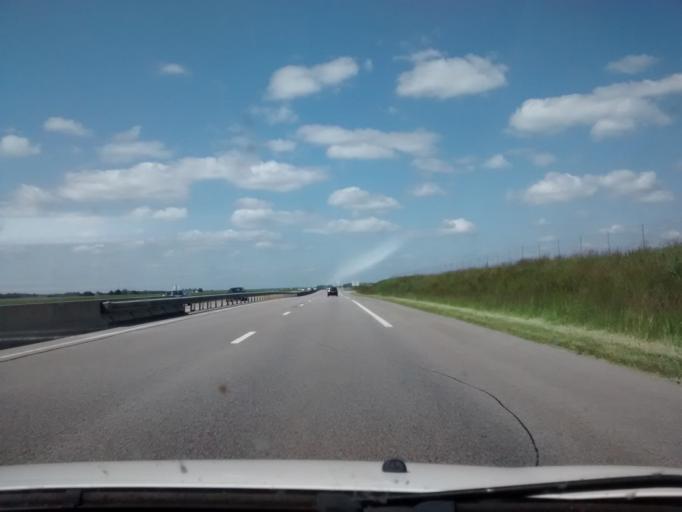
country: FR
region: Ile-de-France
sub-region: Departement des Yvelines
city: Sonchamp
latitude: 48.5729
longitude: 1.8326
